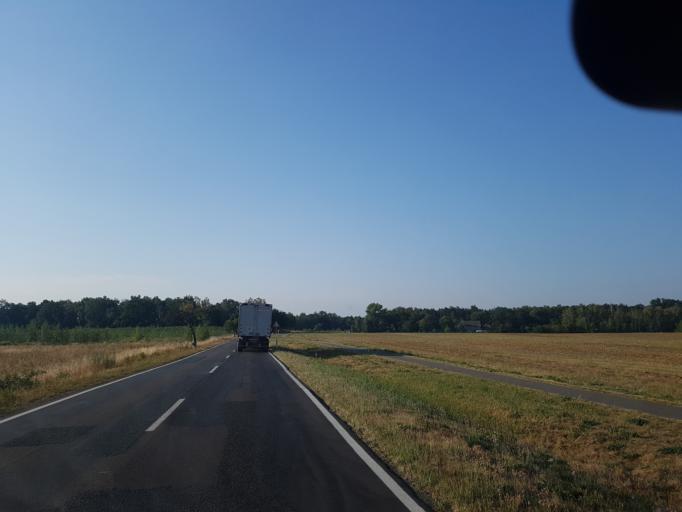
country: DE
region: Brandenburg
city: Hohenleipisch
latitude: 51.4781
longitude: 13.5489
